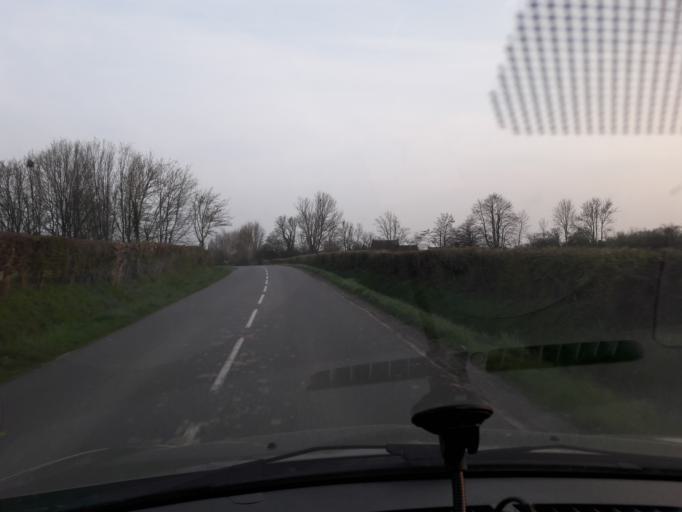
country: FR
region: Nord-Pas-de-Calais
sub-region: Departement du Nord
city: Recquignies
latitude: 50.2646
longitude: 4.0276
